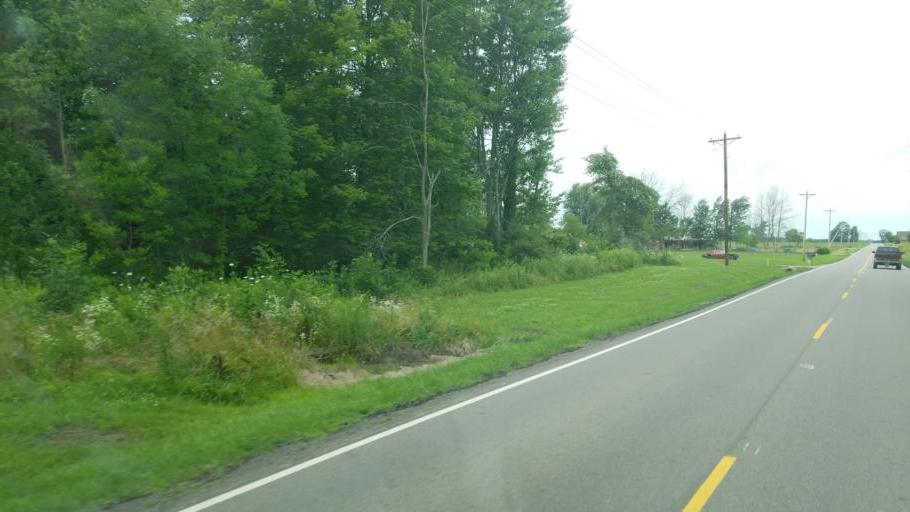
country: US
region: Ohio
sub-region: Licking County
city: Utica
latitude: 40.2317
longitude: -82.5661
